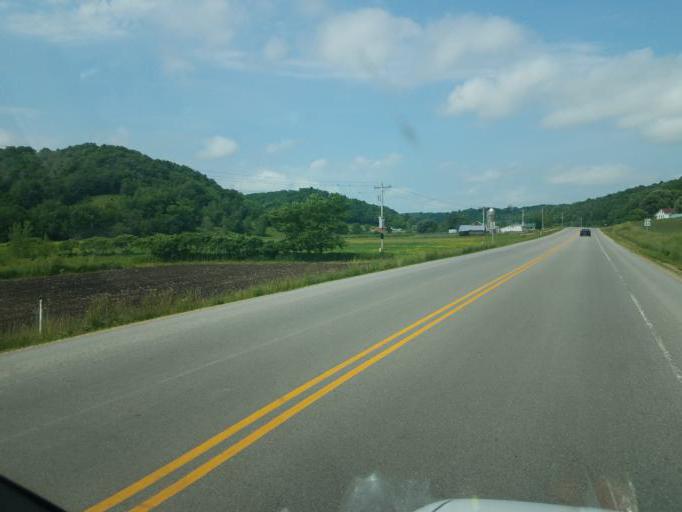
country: US
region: Wisconsin
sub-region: Monroe County
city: Cashton
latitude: 43.7336
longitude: -90.6898
